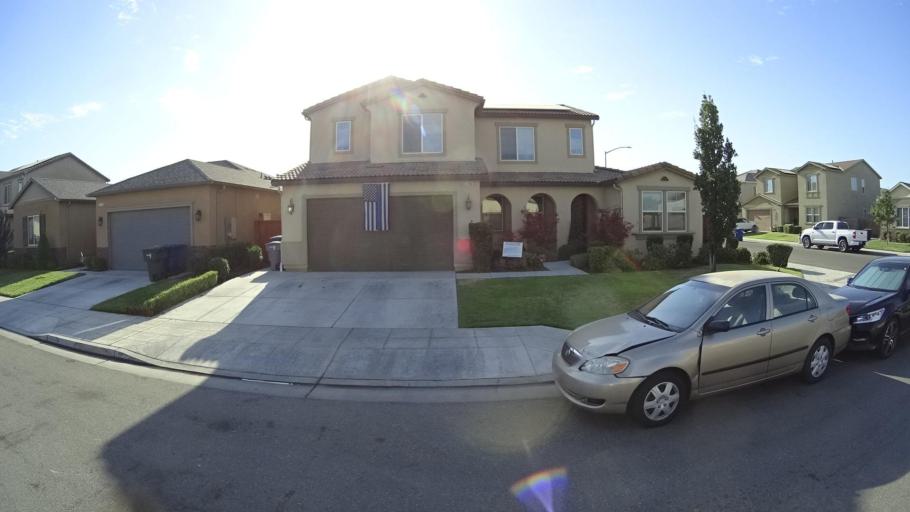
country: US
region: California
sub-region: Fresno County
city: Tarpey Village
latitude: 36.7902
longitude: -119.6709
